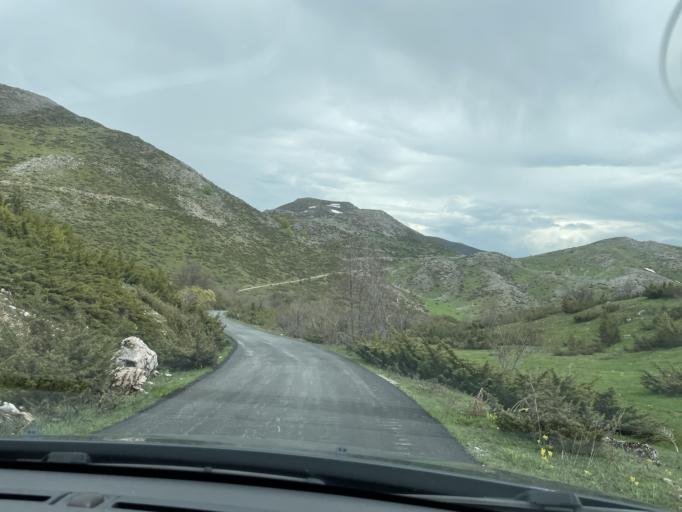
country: MK
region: Opstina Rostusa
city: Rostusha
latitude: 41.6248
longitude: 20.6820
